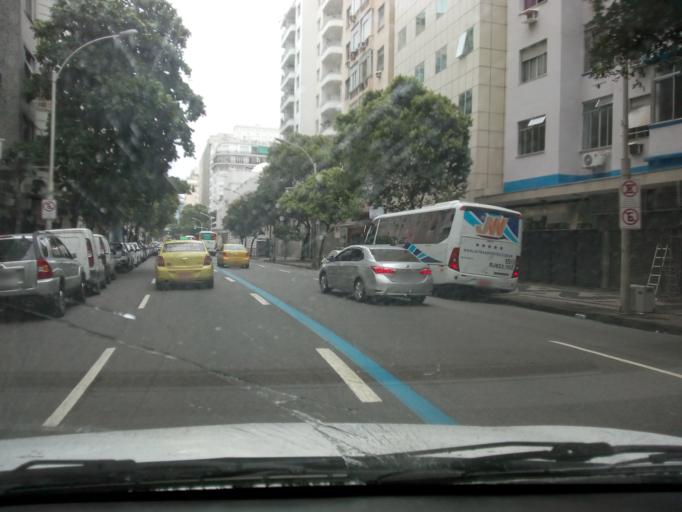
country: BR
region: Rio de Janeiro
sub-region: Rio De Janeiro
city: Rio de Janeiro
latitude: -22.9670
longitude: -43.1806
